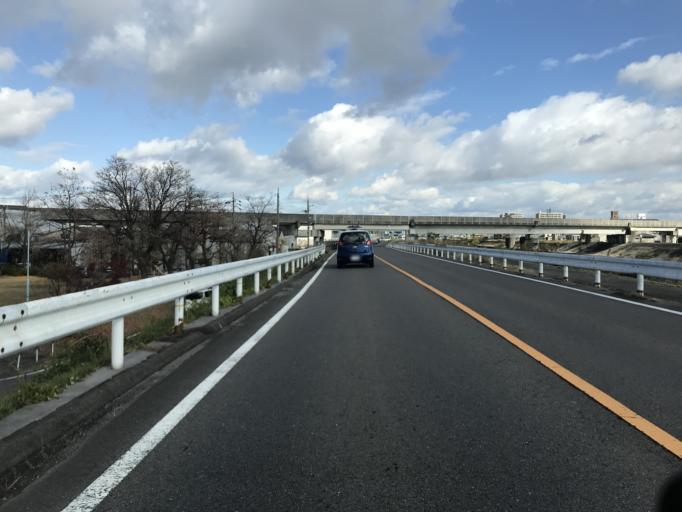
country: JP
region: Aichi
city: Nagoya-shi
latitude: 35.2166
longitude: 136.8667
